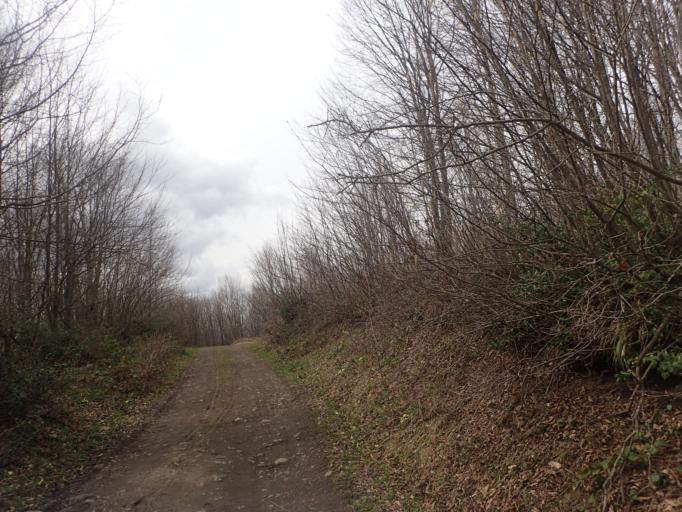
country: TR
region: Ordu
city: Kumru
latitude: 40.8213
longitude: 37.1634
